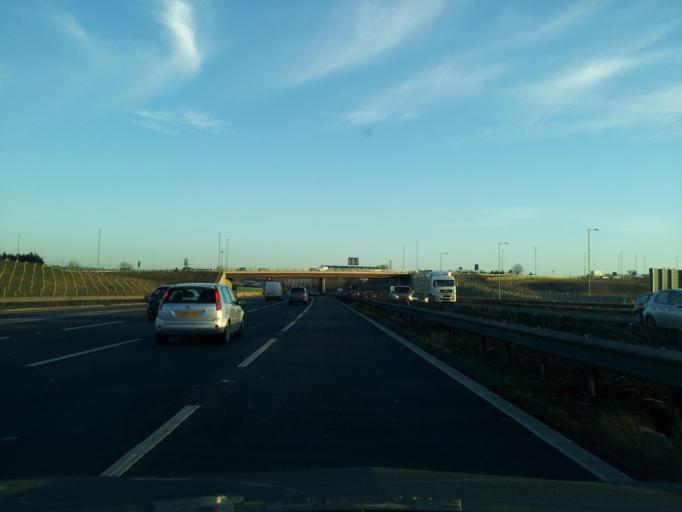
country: GB
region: England
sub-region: Central Bedfordshire
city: Toddington
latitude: 51.9593
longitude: -0.5183
